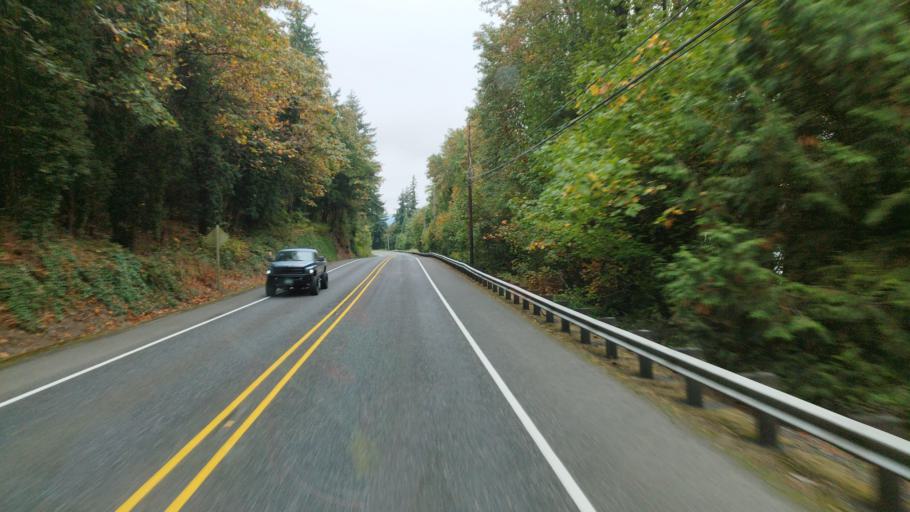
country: US
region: Oregon
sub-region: Columbia County
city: Rainier
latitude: 46.0809
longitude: -122.9125
